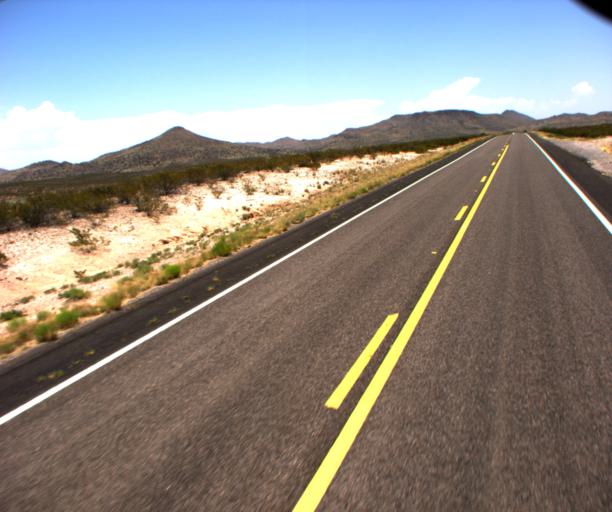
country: US
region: Arizona
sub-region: Greenlee County
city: Clifton
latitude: 32.7535
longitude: -109.3595
